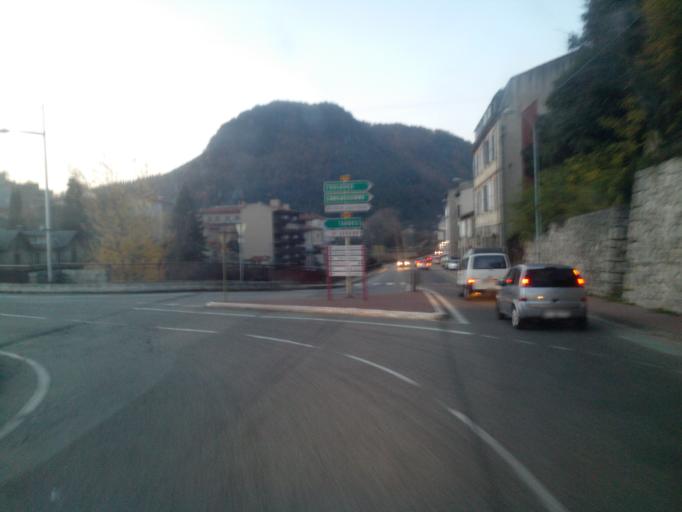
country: FR
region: Midi-Pyrenees
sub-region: Departement de l'Ariege
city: Foix
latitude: 42.9644
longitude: 1.6114
